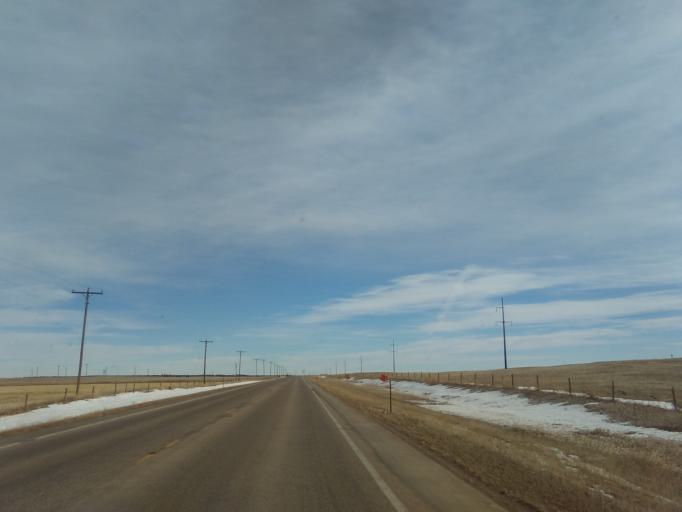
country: US
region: Wyoming
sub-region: Laramie County
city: Ranchettes
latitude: 41.4080
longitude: -104.4443
